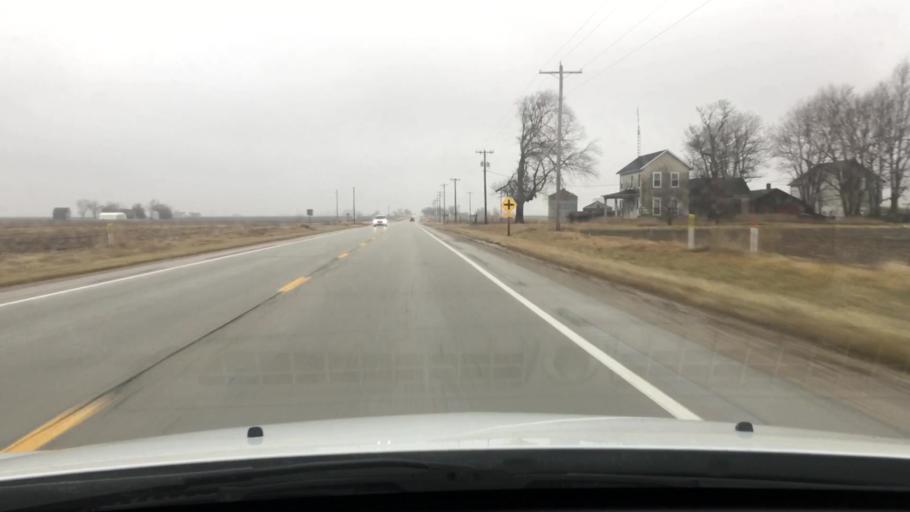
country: US
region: Illinois
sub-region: Livingston County
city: Flanagan
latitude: 40.8721
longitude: -88.7740
